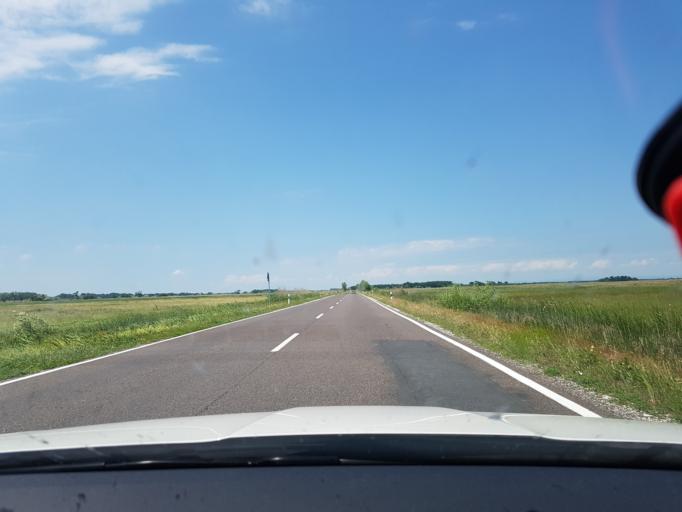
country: HU
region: Hajdu-Bihar
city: Egyek
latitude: 47.5536
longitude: 20.8758
